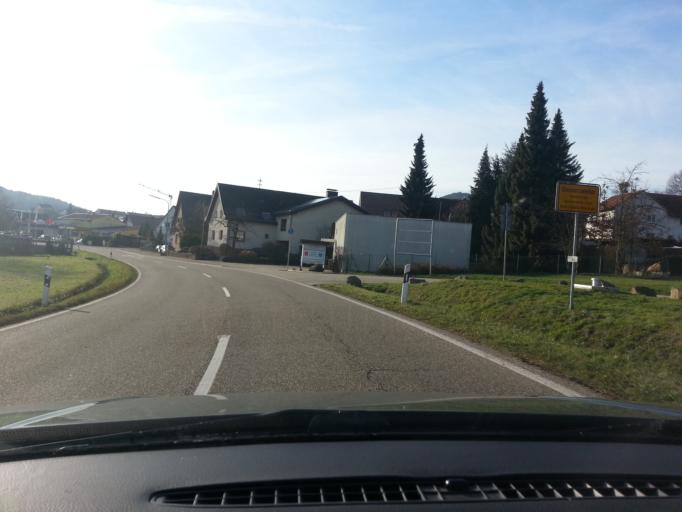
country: DE
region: Rheinland-Pfalz
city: Volkersweiler
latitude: 49.1649
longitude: 7.9314
